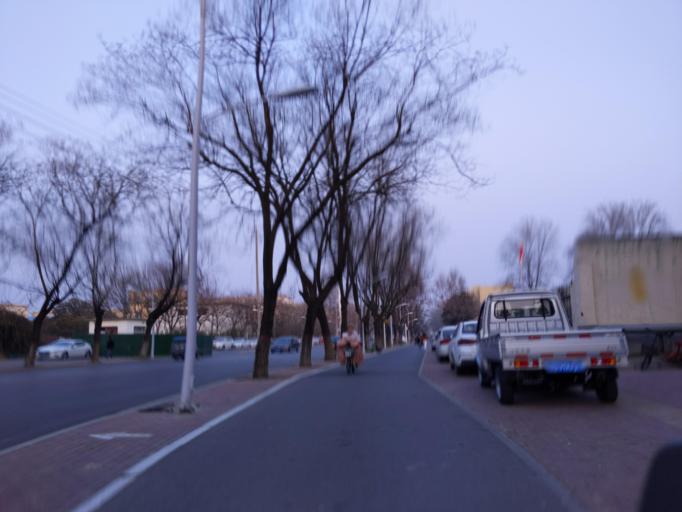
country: CN
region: Henan Sheng
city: Zhongyuanlu
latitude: 35.7696
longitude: 115.0921
